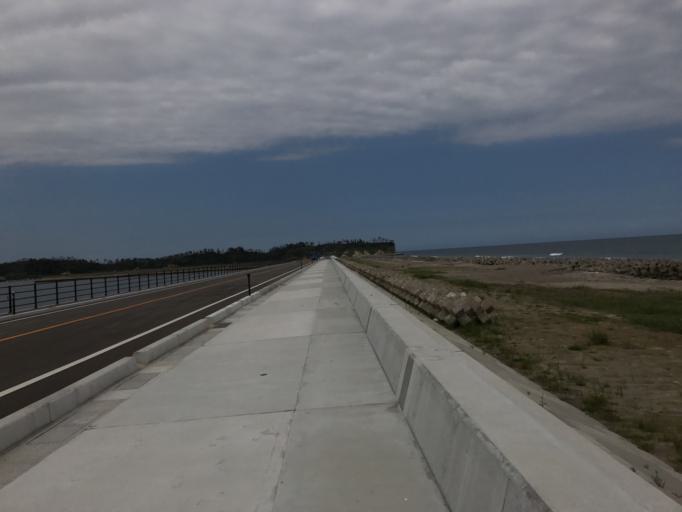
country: JP
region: Miyagi
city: Marumori
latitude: 37.8129
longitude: 140.9855
